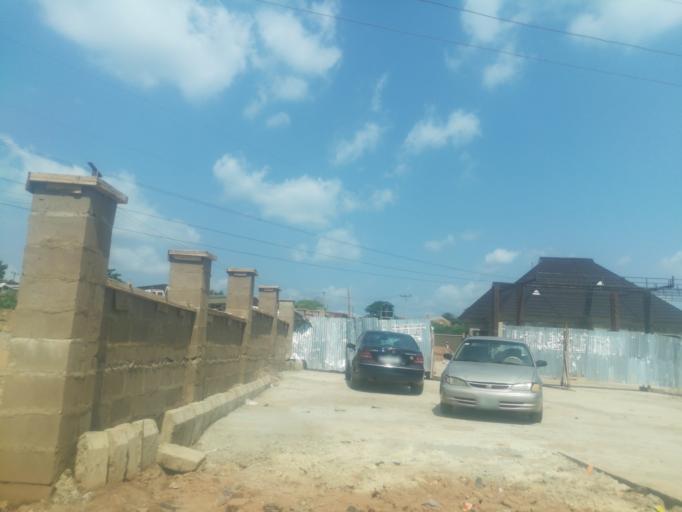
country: NG
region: Oyo
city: Moniya
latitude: 7.5194
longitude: 3.9129
